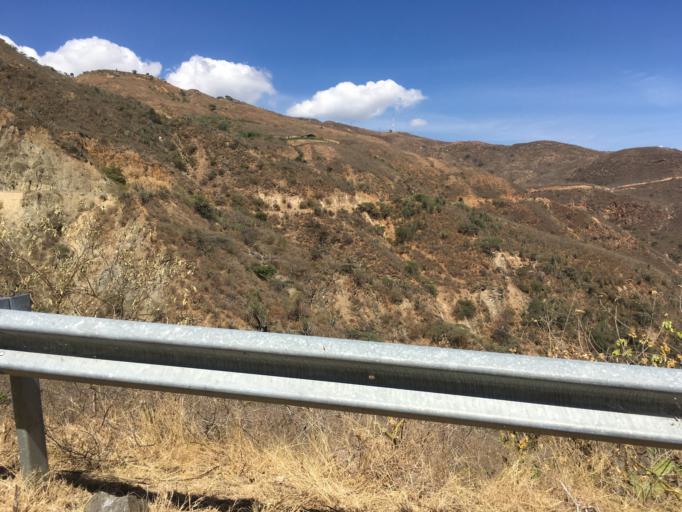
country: CO
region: Santander
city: Aratoca
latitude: 6.7822
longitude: -72.9947
